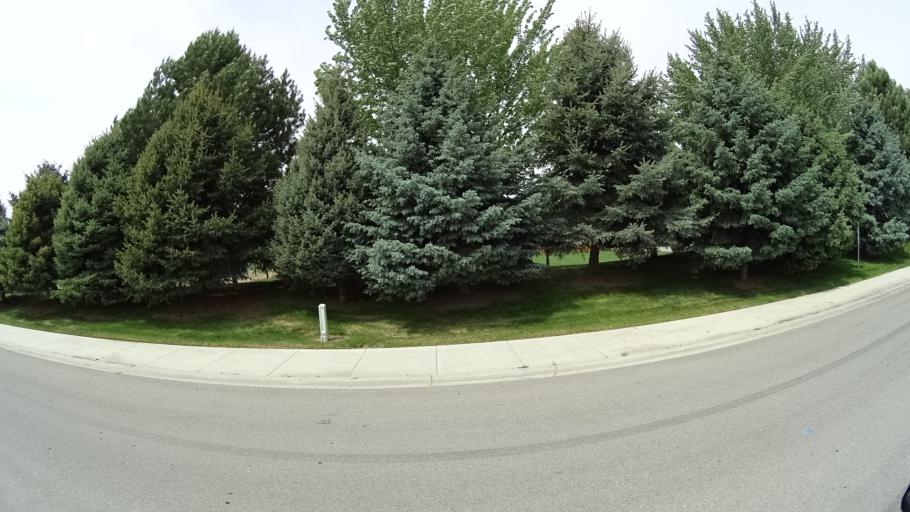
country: US
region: Idaho
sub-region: Ada County
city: Meridian
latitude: 43.5457
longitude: -116.3244
